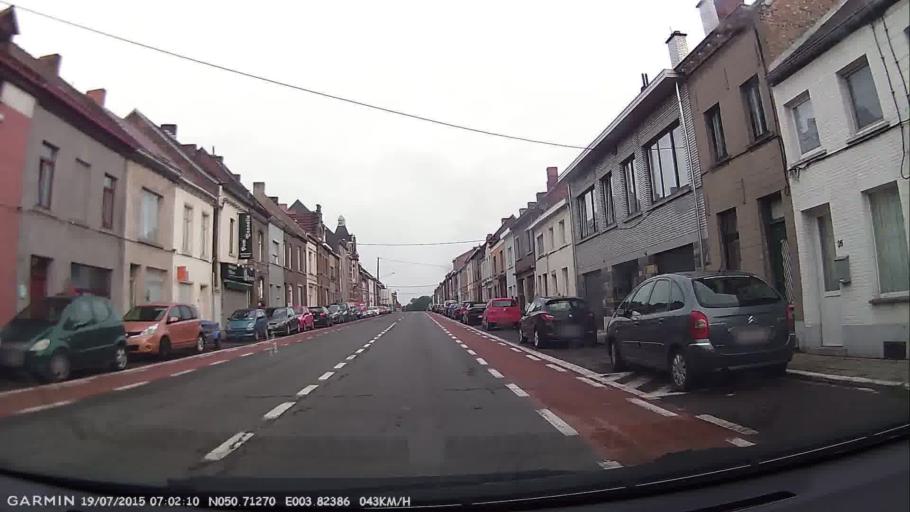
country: BE
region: Wallonia
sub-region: Province du Hainaut
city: Lessines
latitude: 50.7127
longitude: 3.8237
